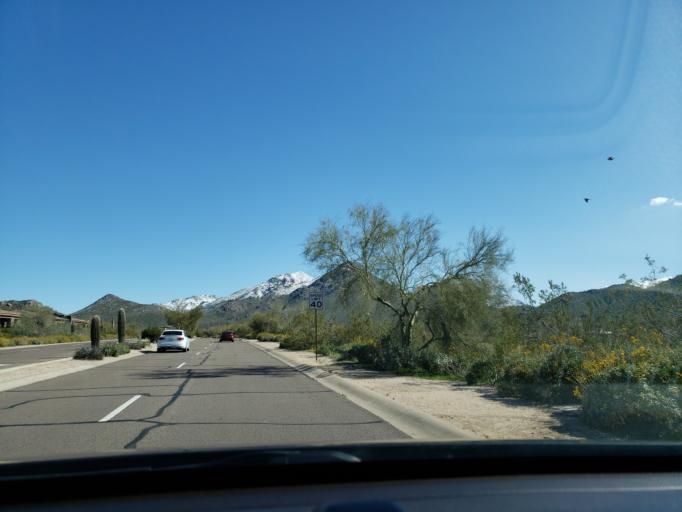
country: US
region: Arizona
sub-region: Maricopa County
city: Carefree
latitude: 33.7088
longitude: -111.8487
